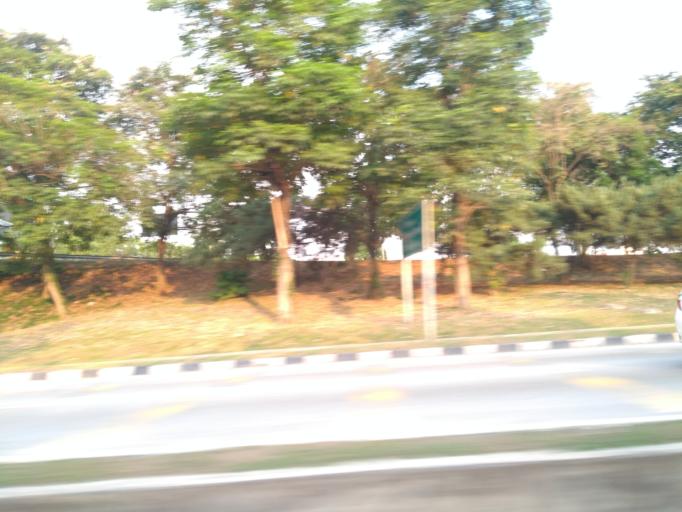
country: MY
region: Kuala Lumpur
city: Kuala Lumpur
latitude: 3.1161
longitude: 101.7069
